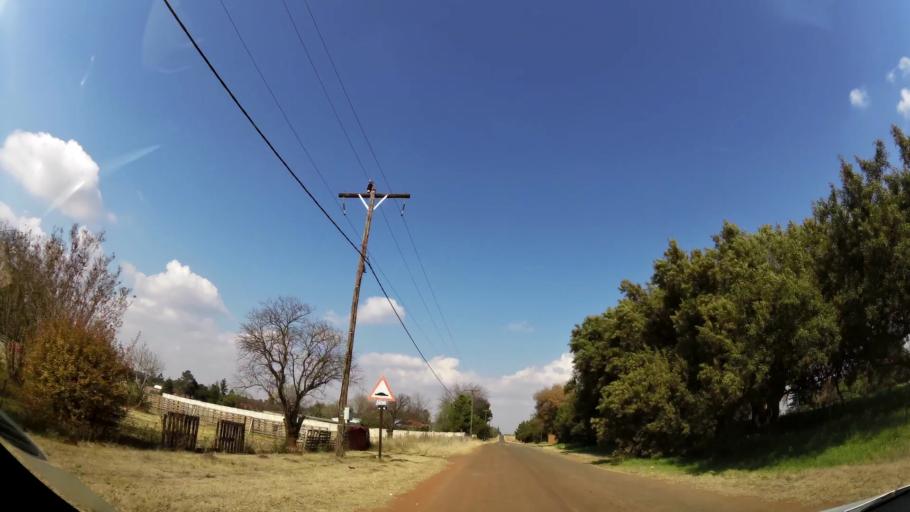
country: ZA
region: Gauteng
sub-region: Ekurhuleni Metropolitan Municipality
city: Springs
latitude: -26.1802
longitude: 28.5338
